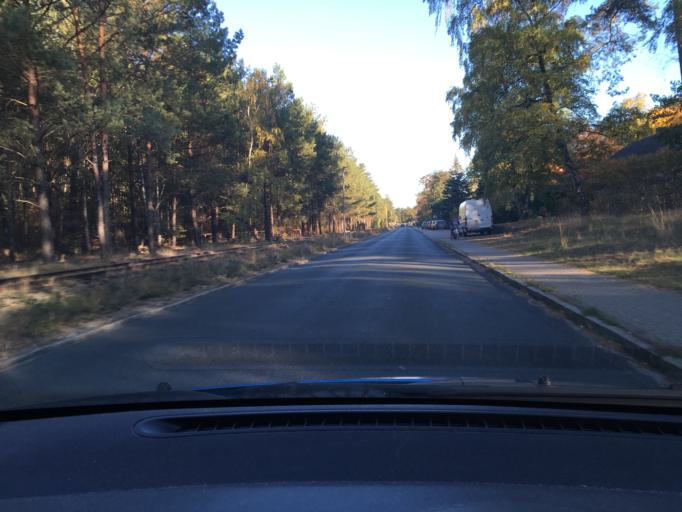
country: DE
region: Lower Saxony
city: Tosterglope
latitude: 53.2659
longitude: 10.7955
